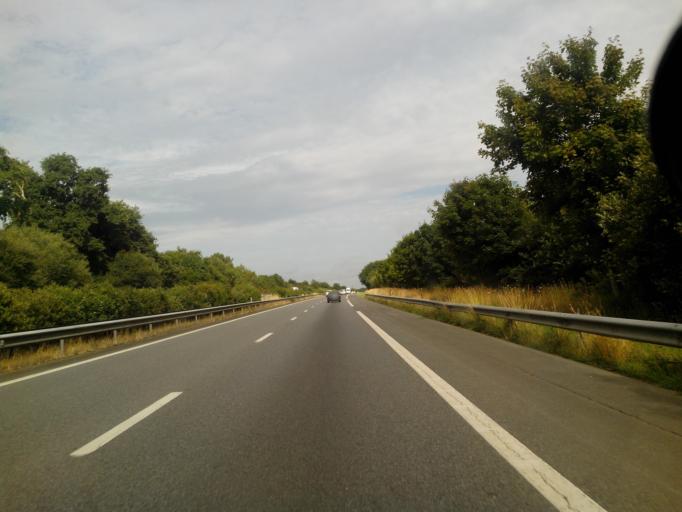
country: FR
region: Pays de la Loire
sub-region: Departement de la Loire-Atlantique
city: La Chapelle-des-Marais
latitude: 47.4876
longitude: -2.2247
